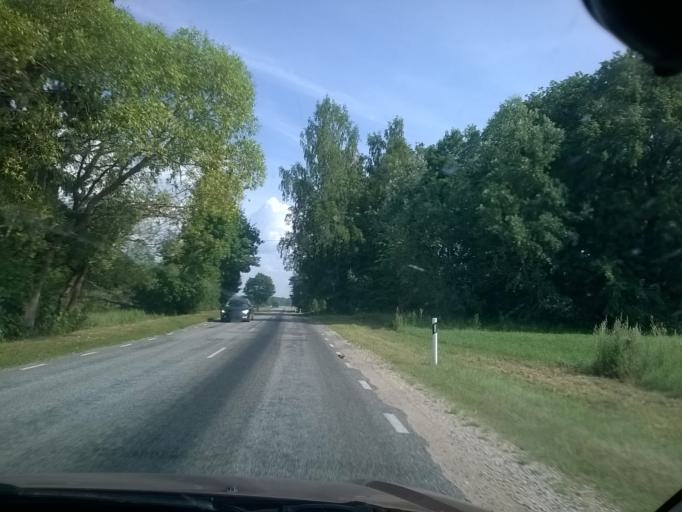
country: EE
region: Tartu
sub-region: Puhja vald
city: Puhja
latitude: 58.2468
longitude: 26.1915
